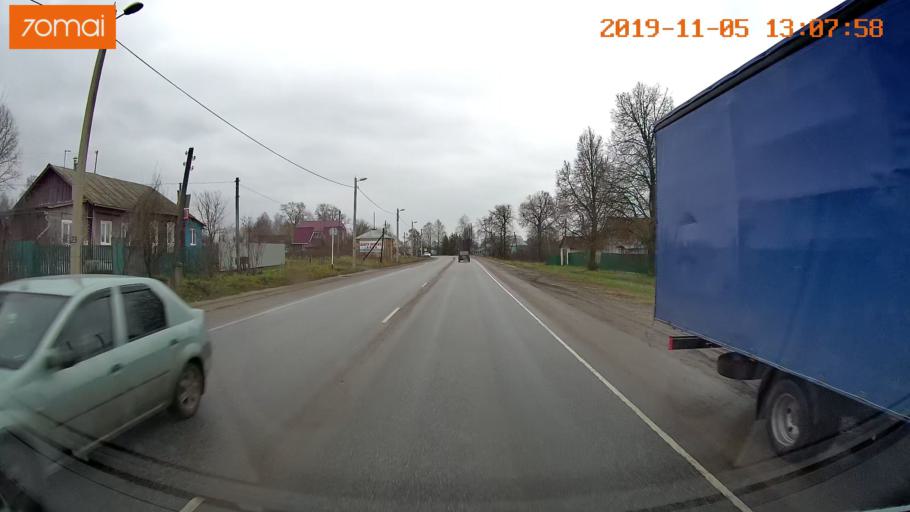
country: RU
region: Ivanovo
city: Kitovo
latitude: 56.8655
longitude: 41.2867
